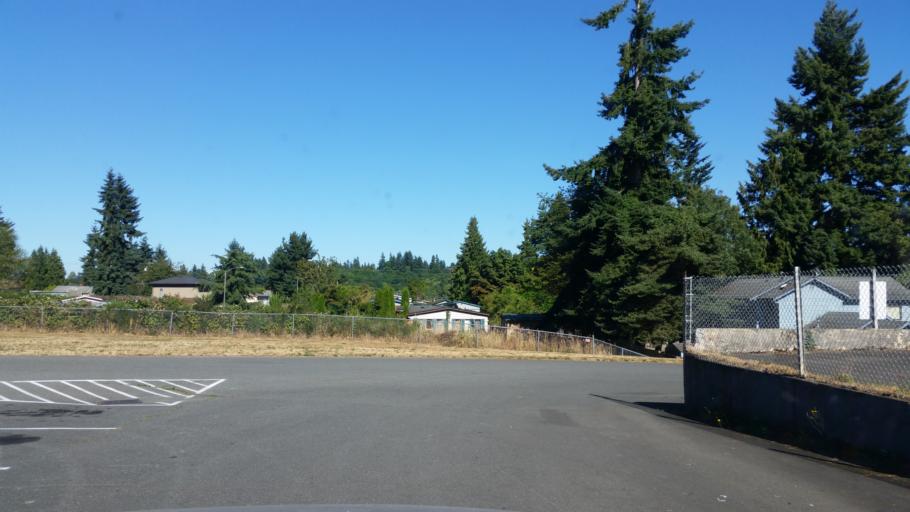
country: US
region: Washington
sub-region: Snohomish County
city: Esperance
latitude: 47.7966
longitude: -122.3384
